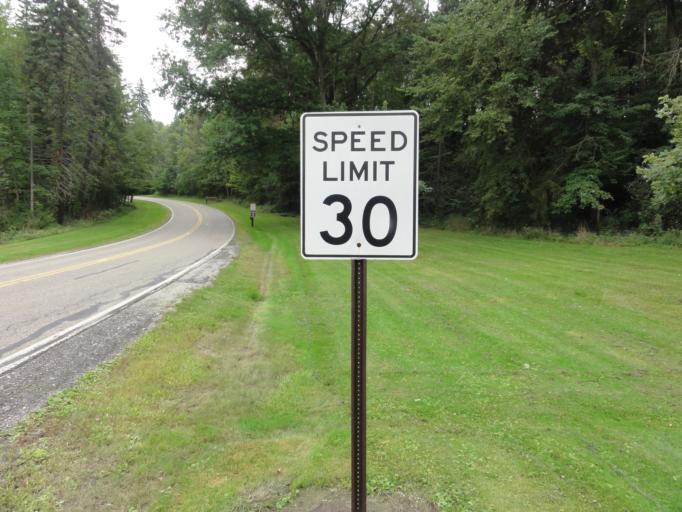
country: US
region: Ohio
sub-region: Cuyahoga County
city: Brecksville
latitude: 41.3150
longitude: -81.6225
